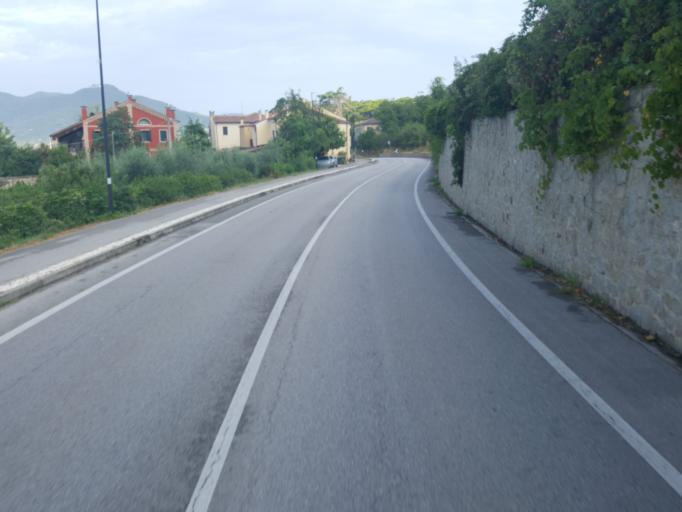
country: IT
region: Veneto
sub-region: Provincia di Padova
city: Battaglia Terme
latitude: 45.2953
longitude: 11.7641
